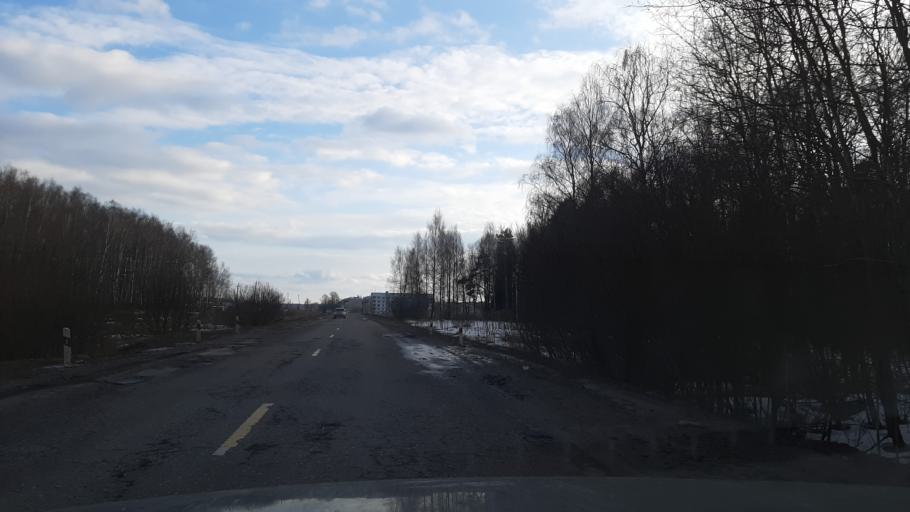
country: RU
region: Ivanovo
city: Novo-Talitsy
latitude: 56.9299
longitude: 40.7354
